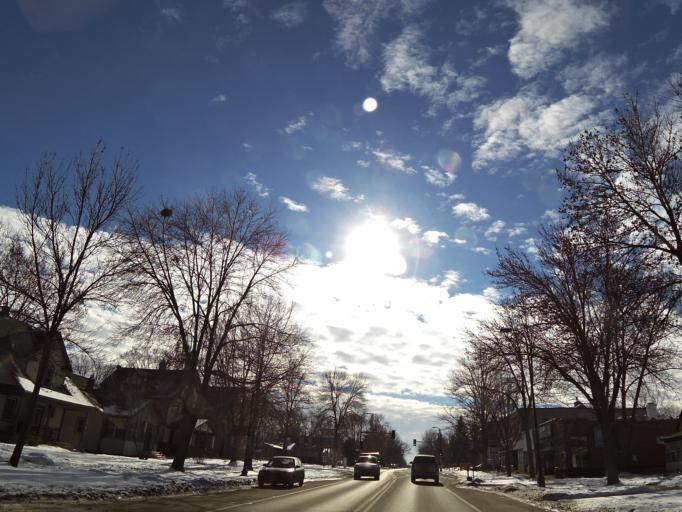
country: US
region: Minnesota
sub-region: Hennepin County
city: Richfield
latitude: 44.9314
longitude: -93.2883
